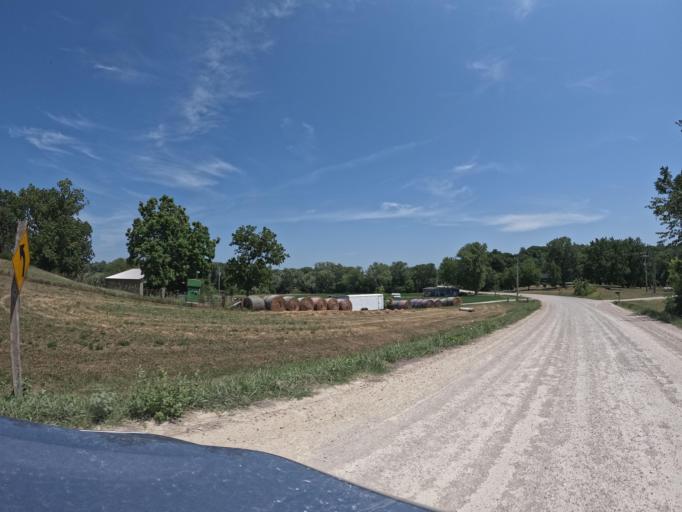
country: US
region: Iowa
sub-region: Henry County
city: Mount Pleasant
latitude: 40.9357
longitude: -91.6230
